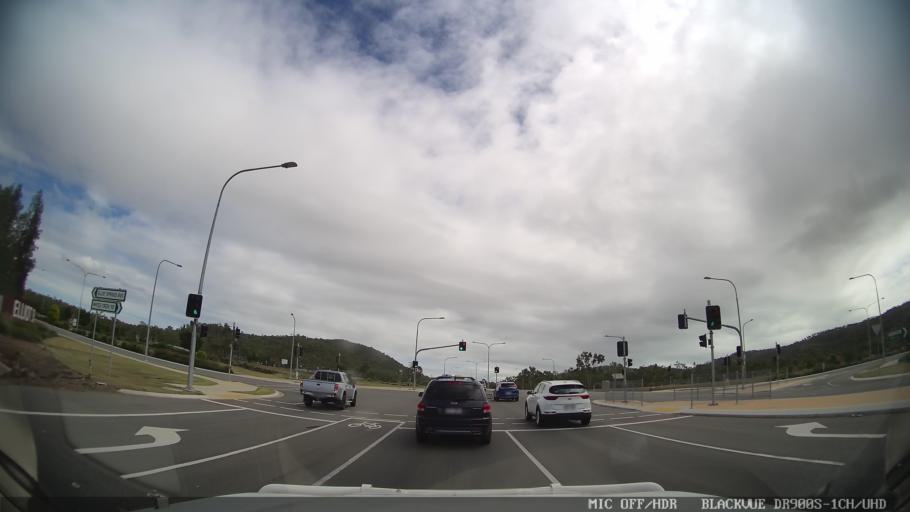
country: AU
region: Queensland
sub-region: Townsville
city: Townsville
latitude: -19.3722
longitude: 146.8991
